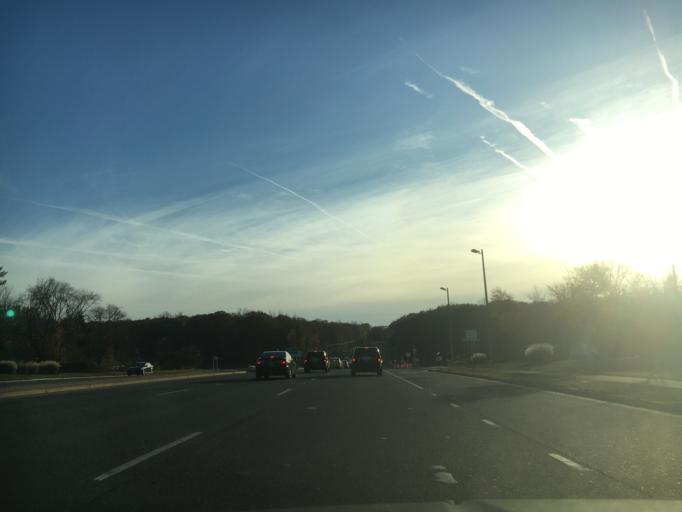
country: US
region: Virginia
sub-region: Prince William County
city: Triangle
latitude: 38.5487
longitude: -77.3351
